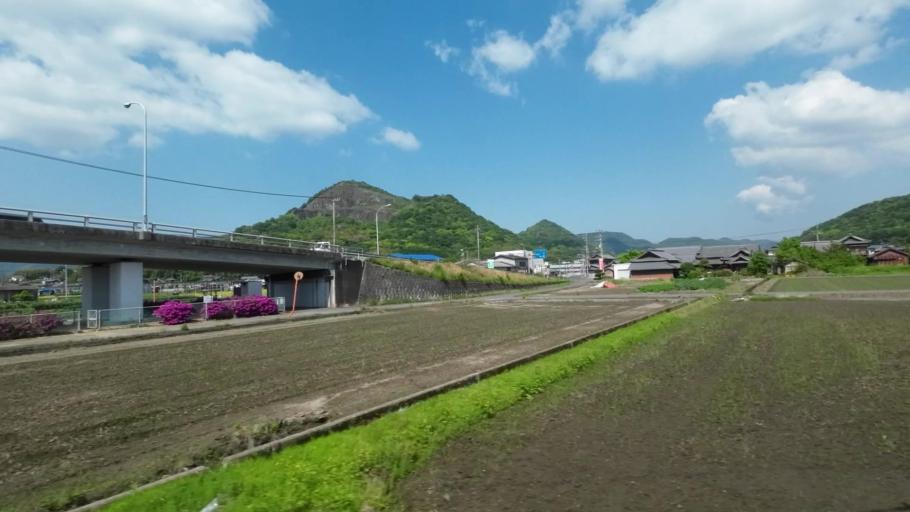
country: JP
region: Kagawa
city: Kan'onjicho
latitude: 34.1885
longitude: 133.7130
